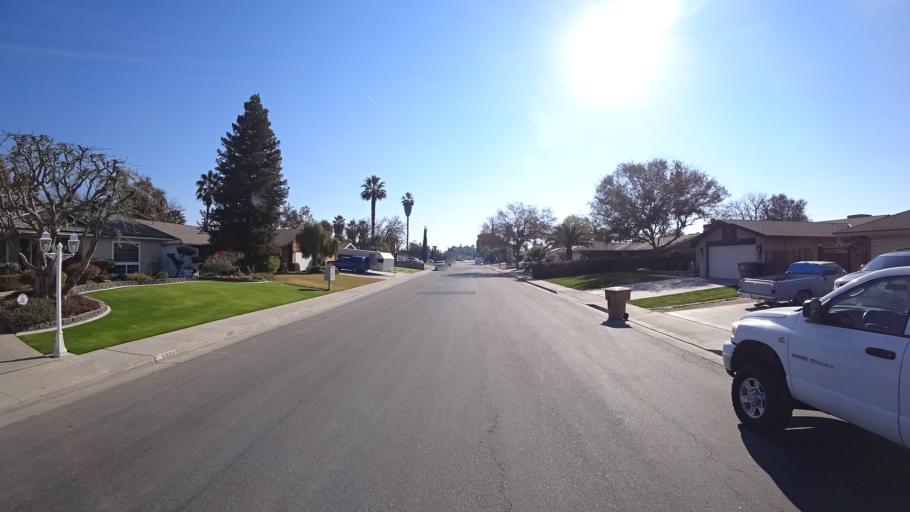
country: US
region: California
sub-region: Kern County
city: Greenfield
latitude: 35.2990
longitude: -119.0368
